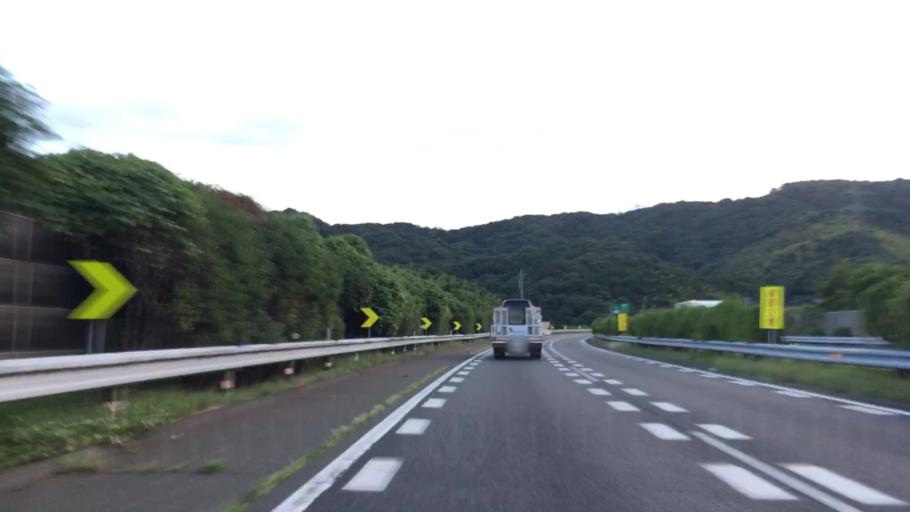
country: JP
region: Yamaguchi
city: Shimonoseki
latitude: 33.9302
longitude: 130.9946
